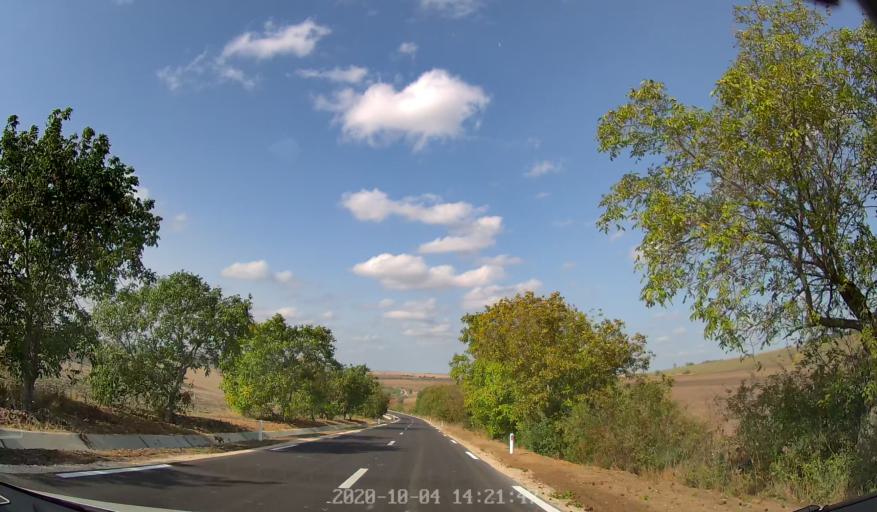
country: MD
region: Rezina
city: Saharna
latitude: 47.5894
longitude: 28.9535
